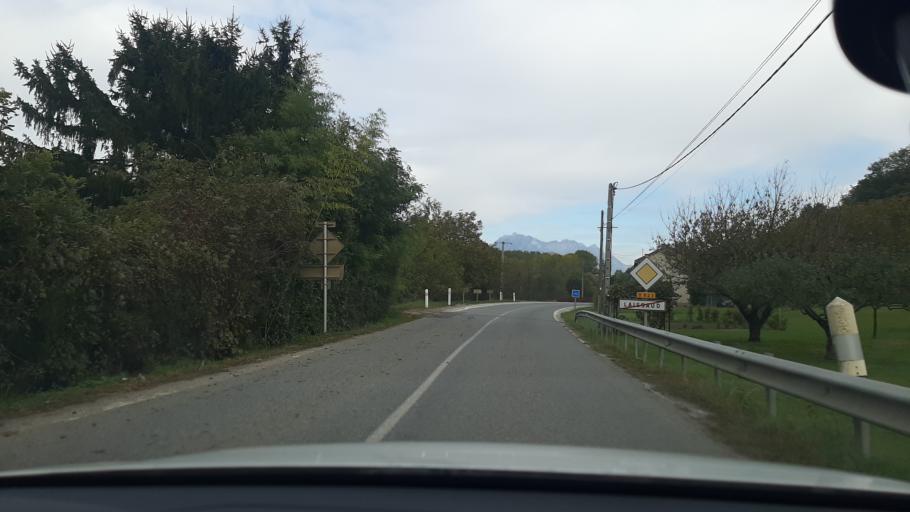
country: FR
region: Rhone-Alpes
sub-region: Departement de l'Isere
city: Pontcharra
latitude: 45.4512
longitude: 6.0422
